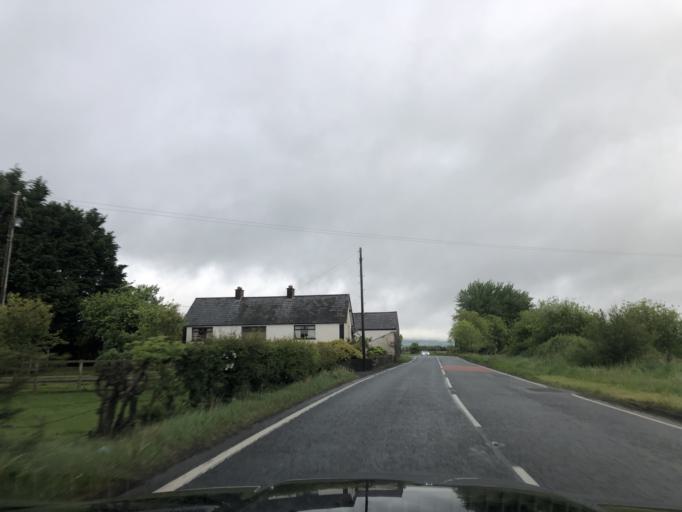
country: GB
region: Northern Ireland
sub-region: Antrim Borough
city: Antrim
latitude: 54.6829
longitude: -6.2242
